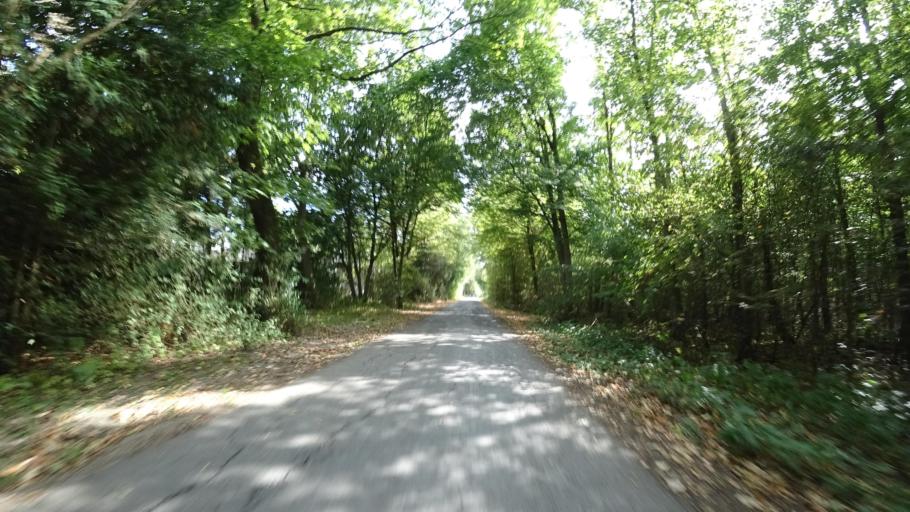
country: DE
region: North Rhine-Westphalia
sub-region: Regierungsbezirk Detmold
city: Rheda-Wiedenbruck
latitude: 51.8503
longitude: 8.2707
